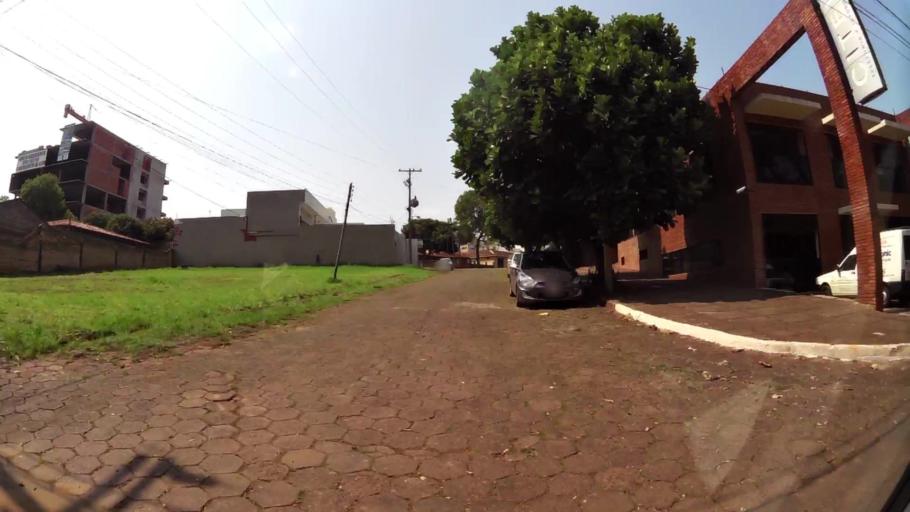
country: PY
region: Alto Parana
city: Presidente Franco
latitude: -25.5204
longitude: -54.6229
